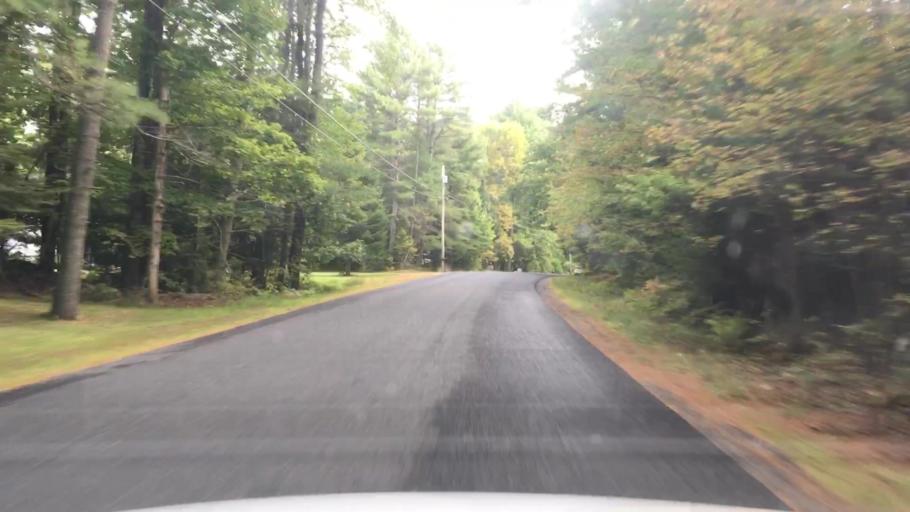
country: US
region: Maine
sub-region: Androscoggin County
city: Lisbon Falls
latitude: 43.9809
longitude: -70.0958
